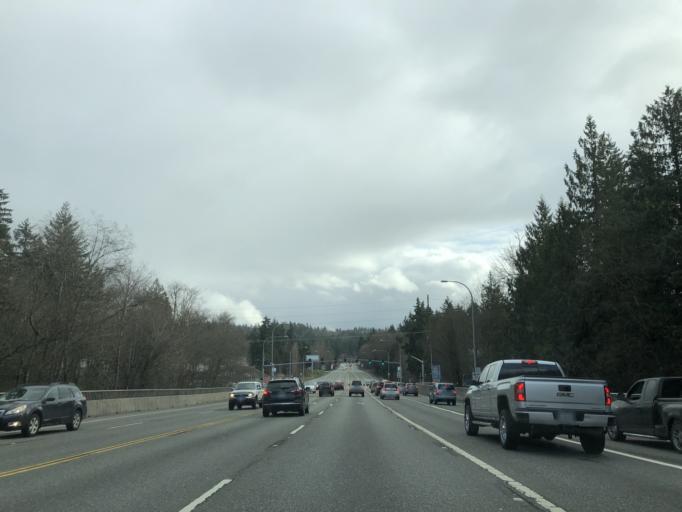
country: US
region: Washington
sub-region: Kitsap County
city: Poulsbo
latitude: 47.7529
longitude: -122.6470
